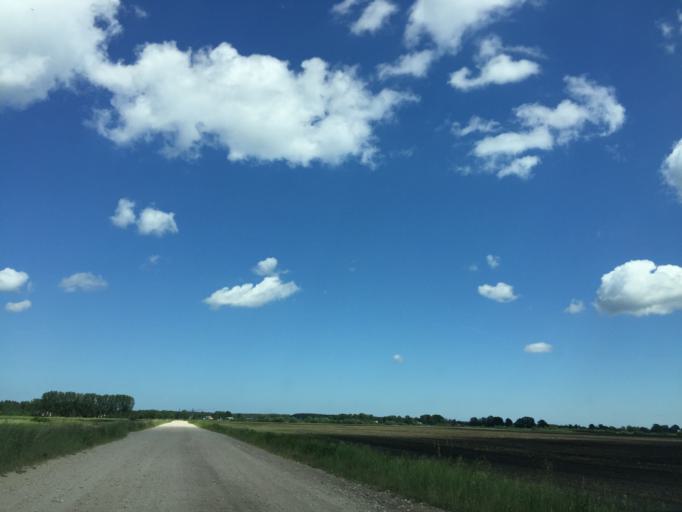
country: LV
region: Olaine
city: Olaine
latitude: 56.8622
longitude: 23.9539
